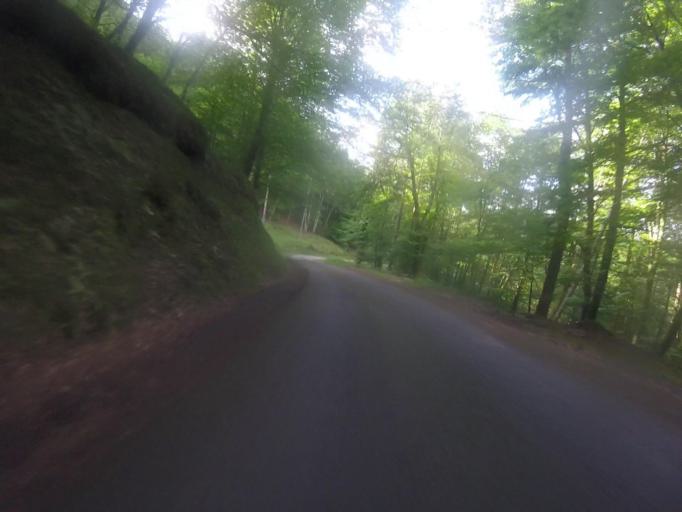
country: ES
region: Navarre
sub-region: Provincia de Navarra
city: Goizueta
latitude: 43.2340
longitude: -1.8055
